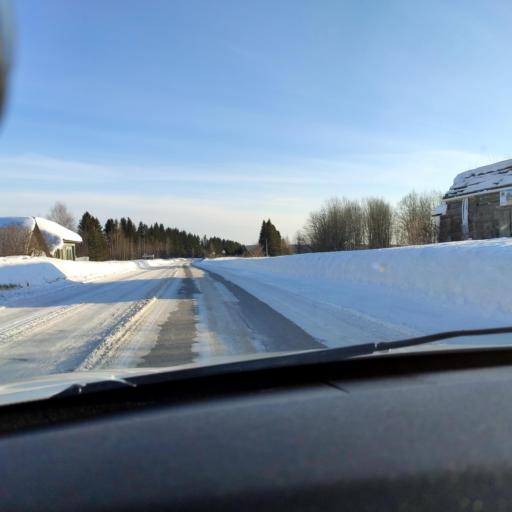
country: RU
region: Perm
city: Polazna
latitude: 58.3258
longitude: 56.4311
